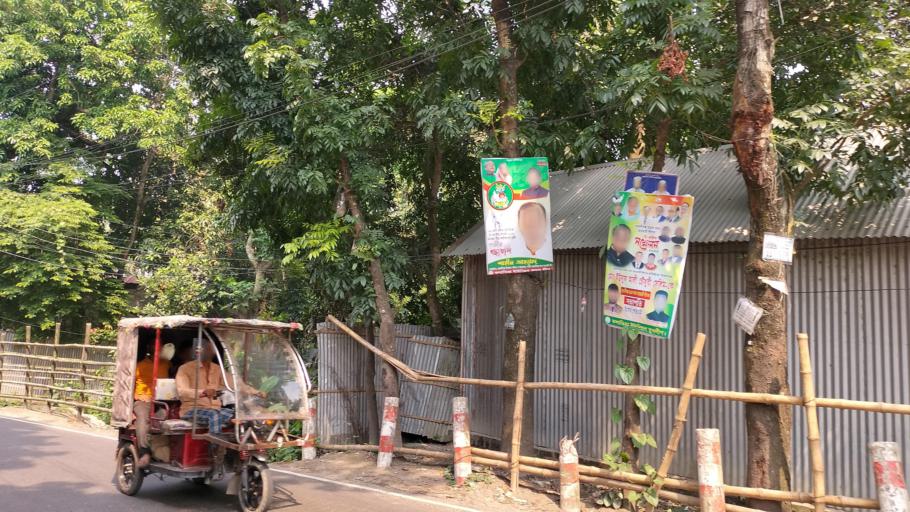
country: BD
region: Dhaka
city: Azimpur
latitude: 23.7001
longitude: 90.2921
